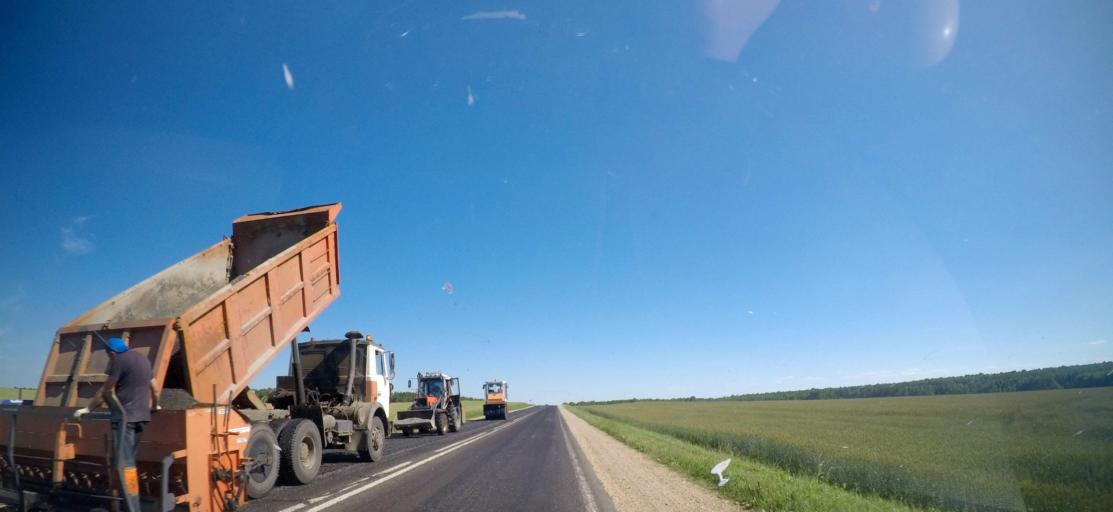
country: BY
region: Grodnenskaya
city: Vyalikaya Byerastavitsa
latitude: 53.2250
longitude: 23.9926
